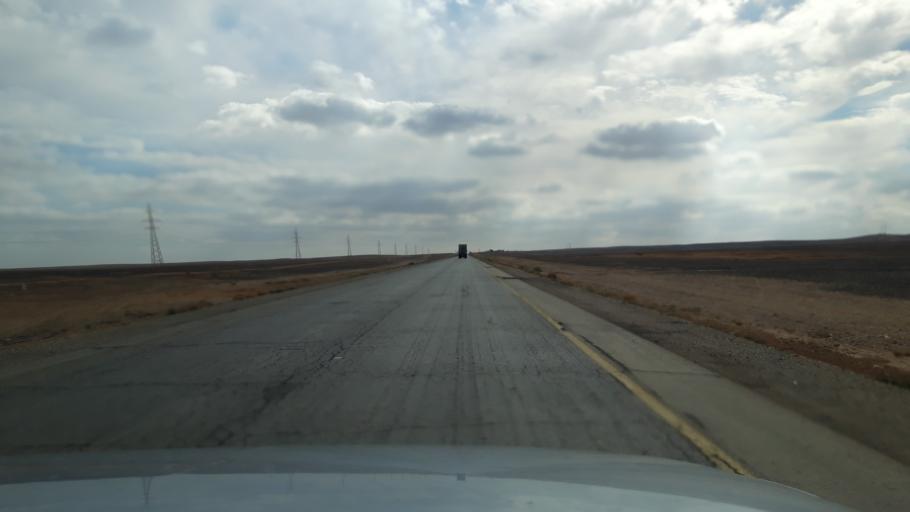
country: JO
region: Amman
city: Al Azraq ash Shamali
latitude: 31.7624
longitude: 36.5545
